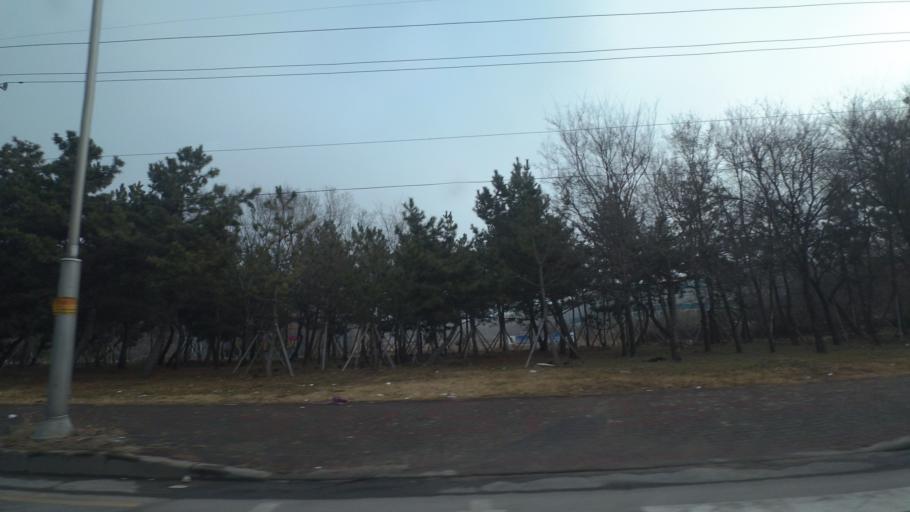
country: KR
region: Gyeonggi-do
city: Hwaseong-si
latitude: 36.9906
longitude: 126.8519
